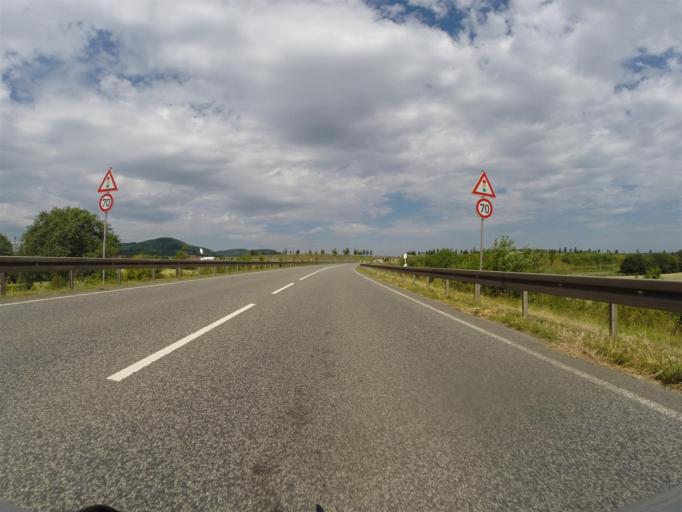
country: DE
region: Thuringia
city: Niedergebra
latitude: 51.4304
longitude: 10.6016
